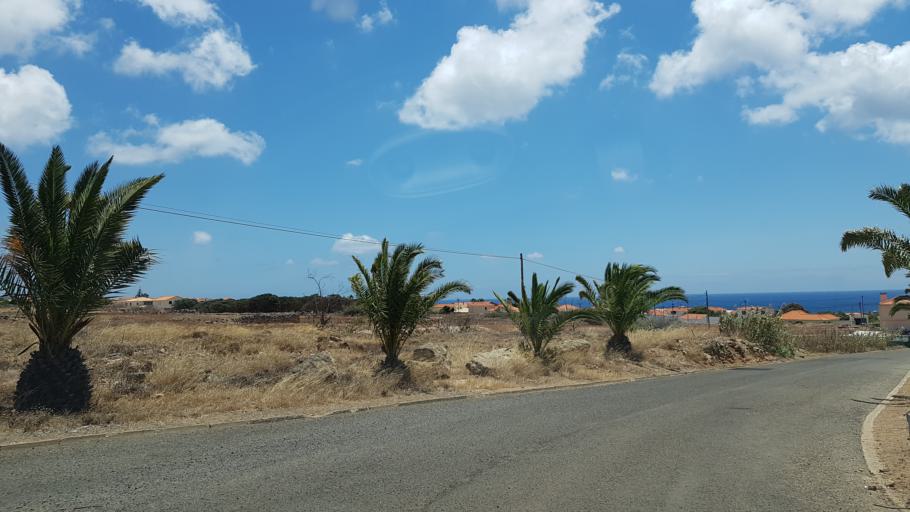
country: PT
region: Madeira
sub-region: Porto Santo
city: Vila de Porto Santo
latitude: 33.0631
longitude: -16.3611
